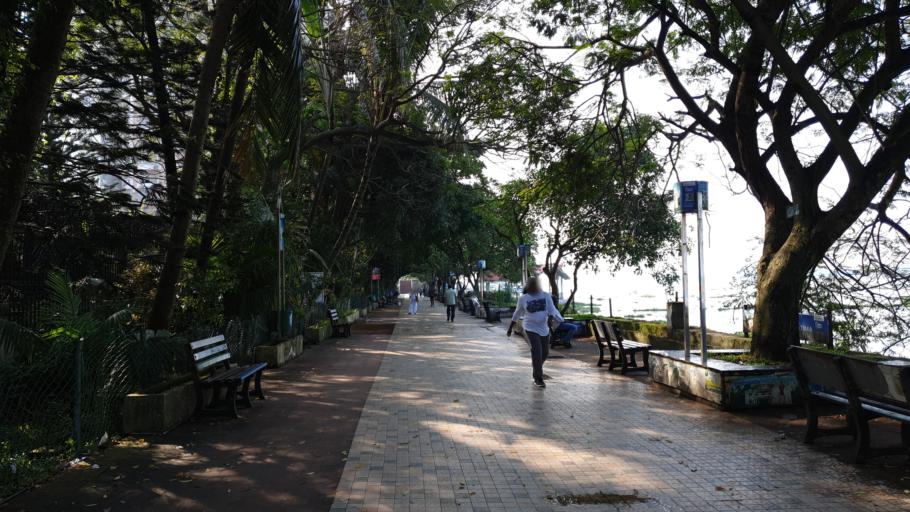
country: IN
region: Kerala
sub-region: Ernakulam
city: Cochin
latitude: 9.9763
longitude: 76.2768
